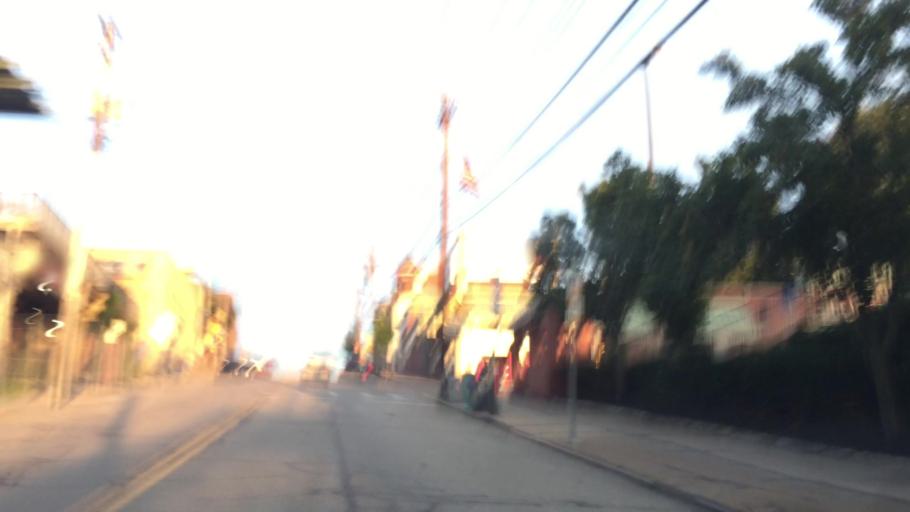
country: US
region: Pennsylvania
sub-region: Allegheny County
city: Pittsburgh
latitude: 40.4300
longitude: -80.0084
